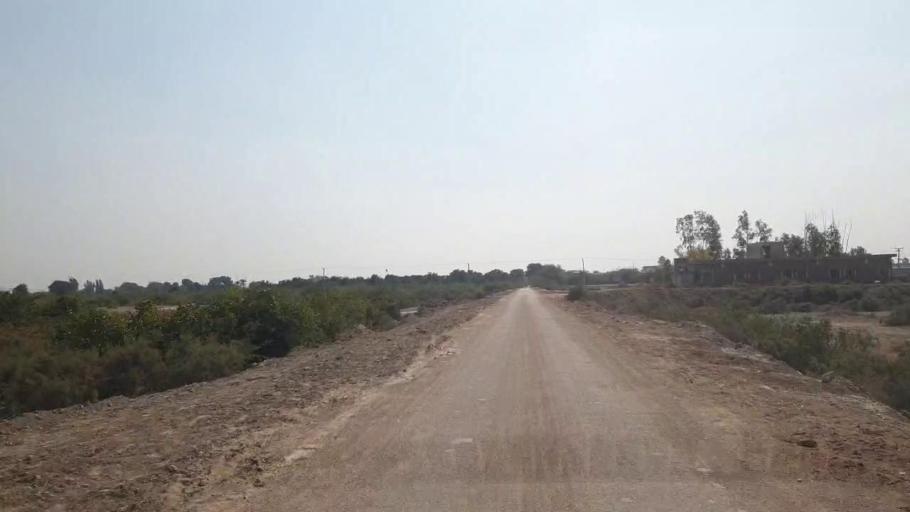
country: PK
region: Sindh
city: Chambar
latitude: 25.3776
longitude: 68.8808
